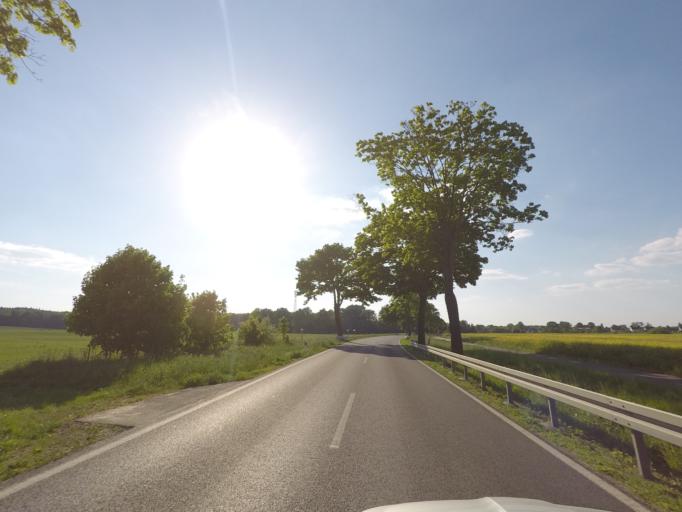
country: DE
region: Brandenburg
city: Hohenfinow
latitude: 52.8202
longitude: 13.8762
